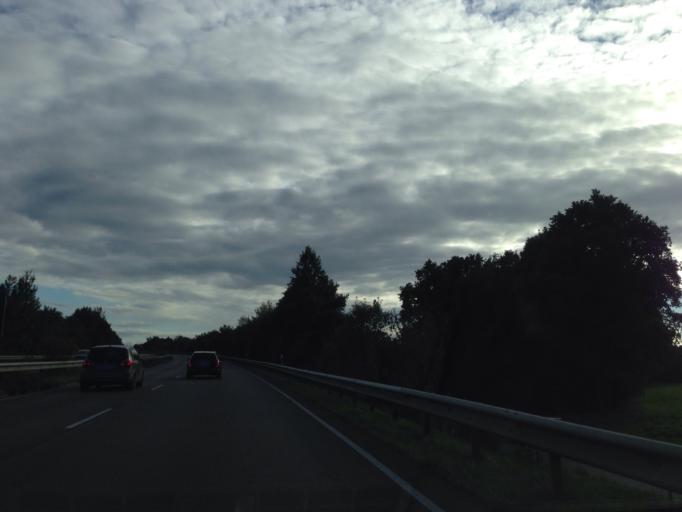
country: DE
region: Lower Saxony
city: Wendisch Evern
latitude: 53.2236
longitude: 10.4475
